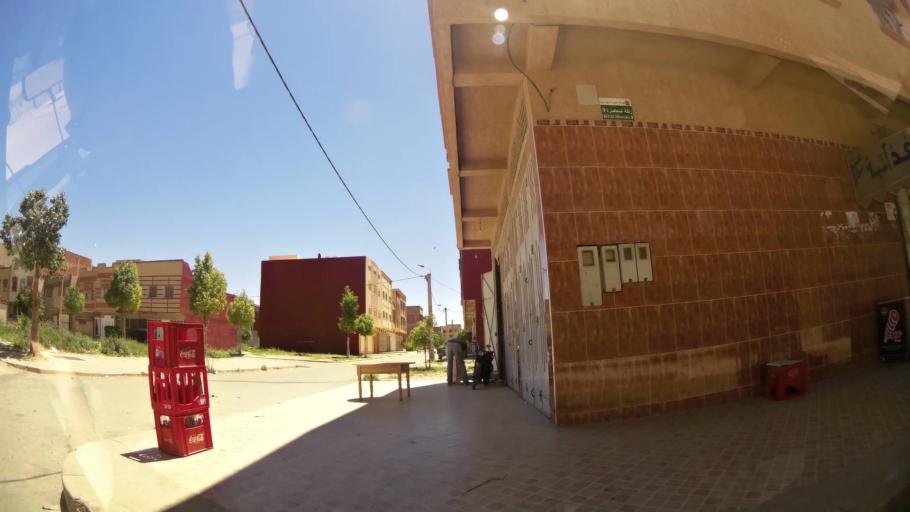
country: MA
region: Oriental
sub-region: Oujda-Angad
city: Oujda
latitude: 34.6772
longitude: -1.8612
